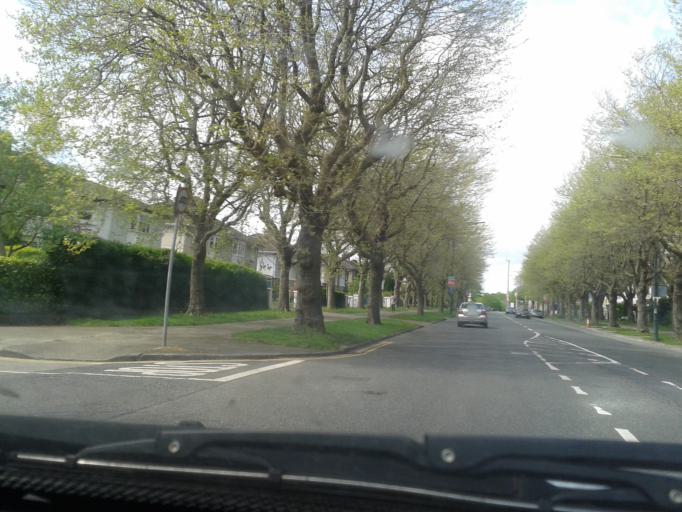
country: IE
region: Leinster
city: Glasnevin
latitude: 53.3781
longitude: -6.2624
